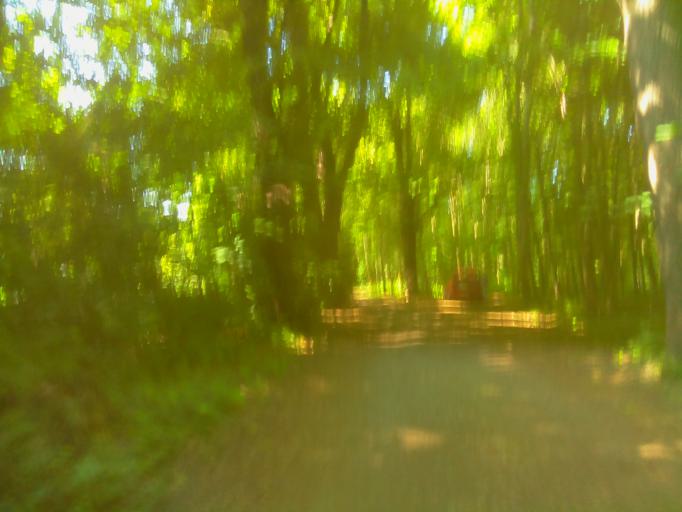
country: DE
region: Thuringia
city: Rudolstadt
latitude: 50.7145
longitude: 11.3240
